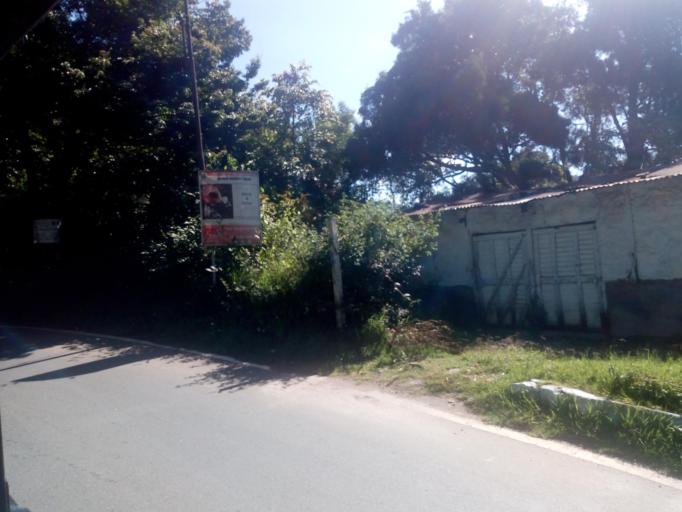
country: IN
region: Tamil Nadu
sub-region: Nilgiri
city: Wellington
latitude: 11.3453
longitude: 76.7900
